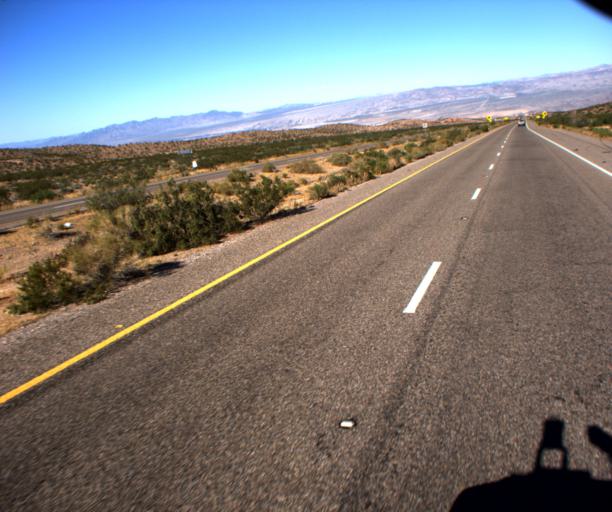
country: US
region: Nevada
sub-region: Clark County
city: Laughlin
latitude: 35.1856
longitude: -114.4608
